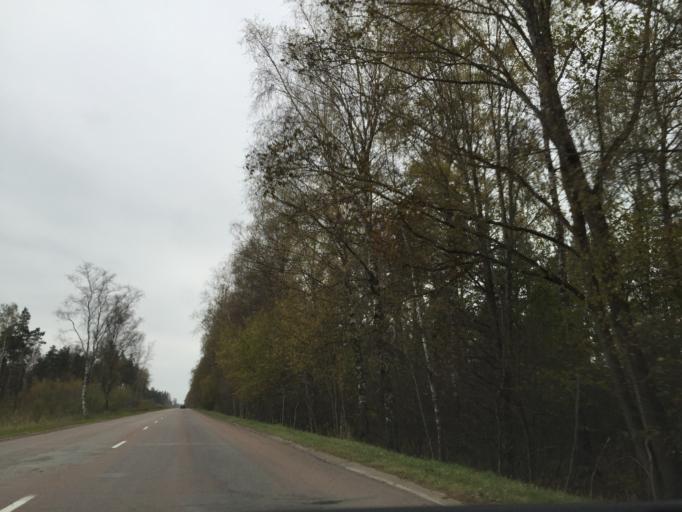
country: LV
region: Marupe
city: Marupe
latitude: 56.8761
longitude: 24.0660
